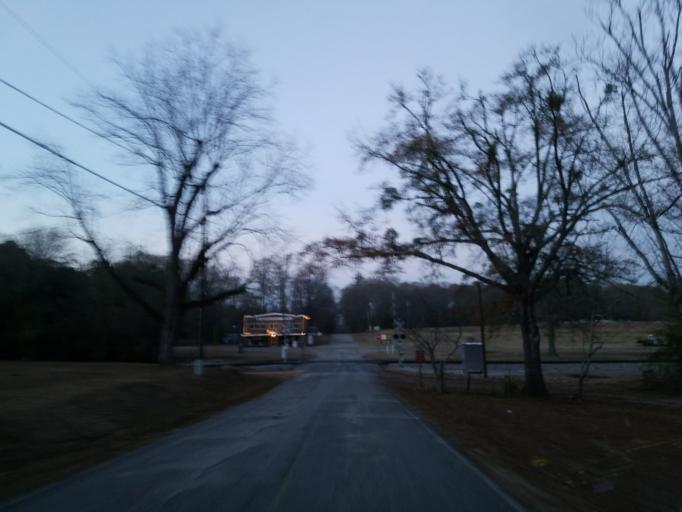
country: US
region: Alabama
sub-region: Sumter County
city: York
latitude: 32.4232
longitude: -88.4382
